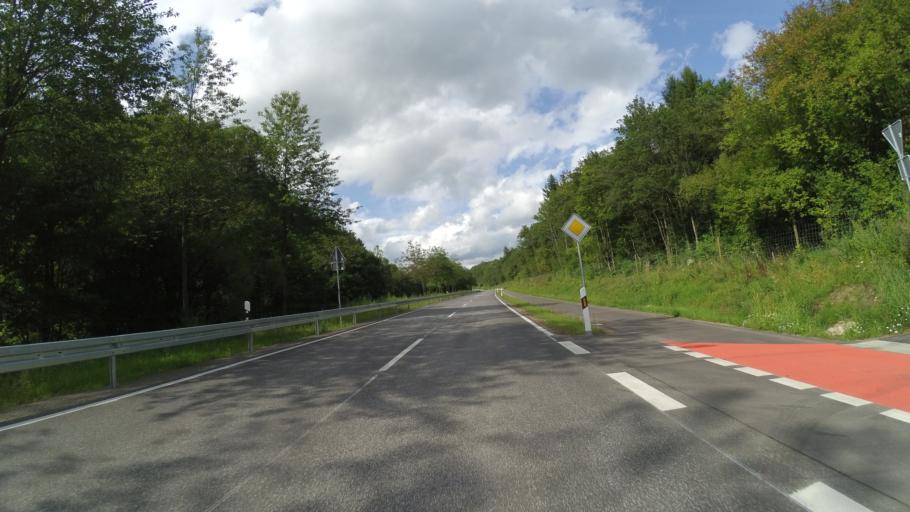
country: DE
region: Saarland
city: Nonnweiler
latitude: 49.5614
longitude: 6.9699
